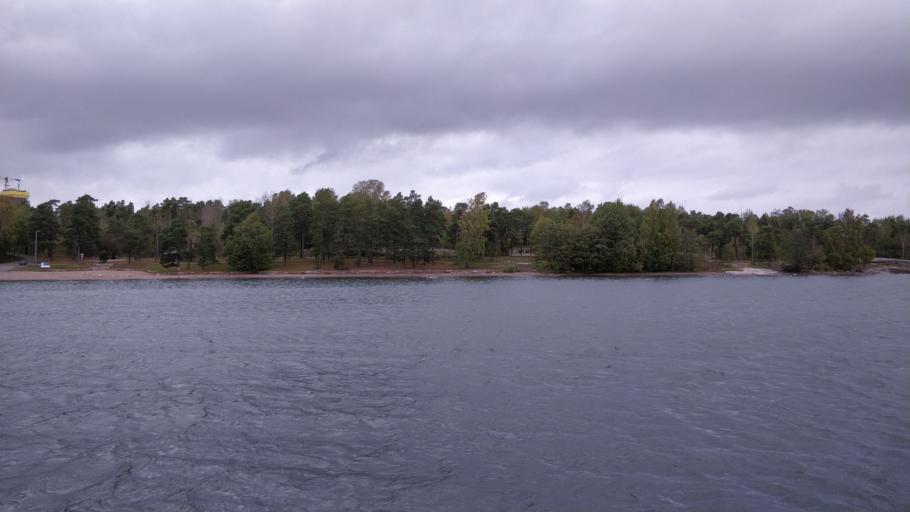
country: FI
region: Uusimaa
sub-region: Helsinki
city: Helsinki
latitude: 60.1776
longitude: 24.9955
